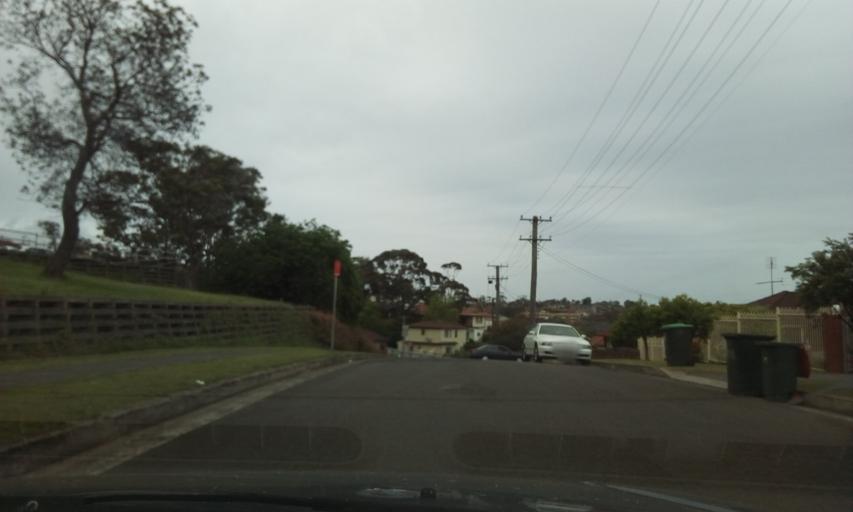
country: AU
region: New South Wales
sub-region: Wollongong
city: Lake Heights
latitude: -34.4865
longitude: 150.8823
